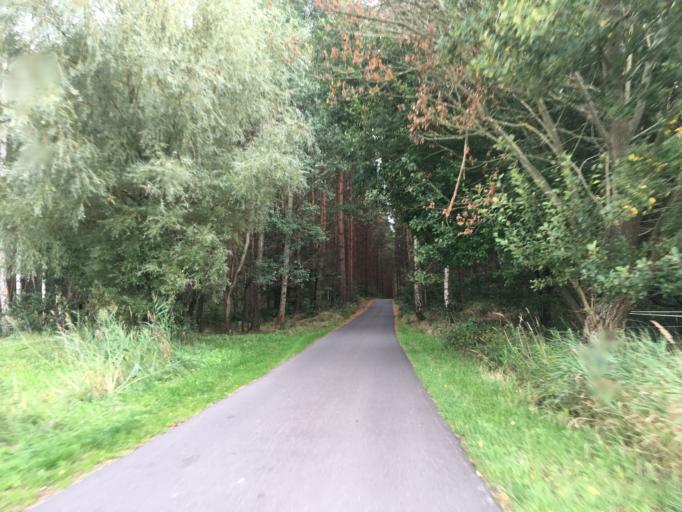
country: DE
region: Brandenburg
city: Friedrichswalde
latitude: 53.0170
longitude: 13.7313
